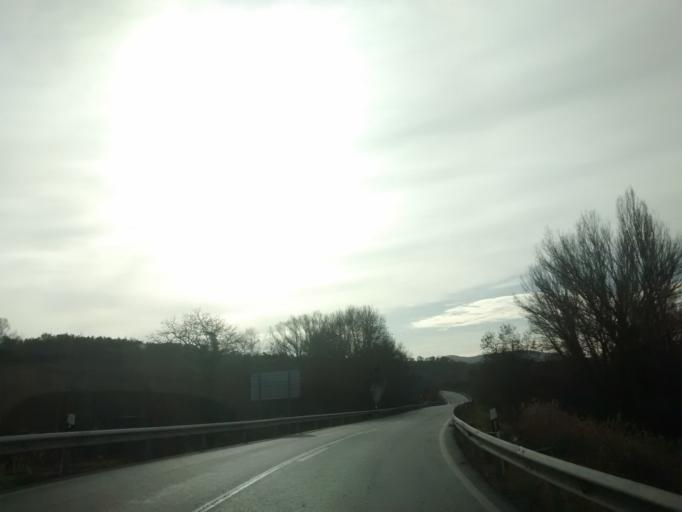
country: ES
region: Aragon
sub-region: Provincia de Zaragoza
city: Mianos
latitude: 42.6131
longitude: -0.9025
